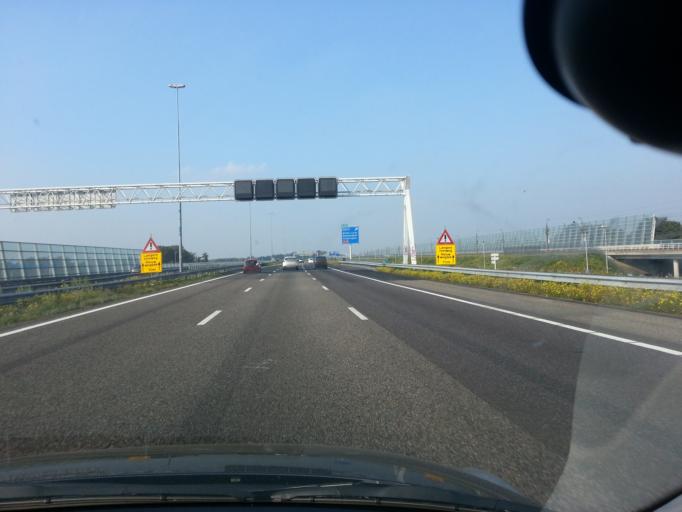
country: NL
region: North Brabant
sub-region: Gemeente Breda
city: Breda
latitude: 51.5626
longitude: 4.7335
